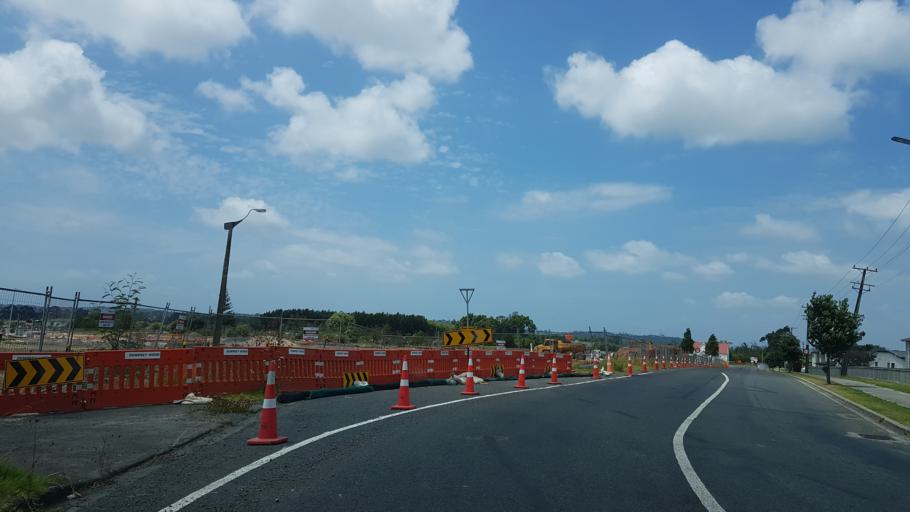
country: NZ
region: Auckland
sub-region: Auckland
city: Rosebank
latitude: -36.7988
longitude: 174.6527
